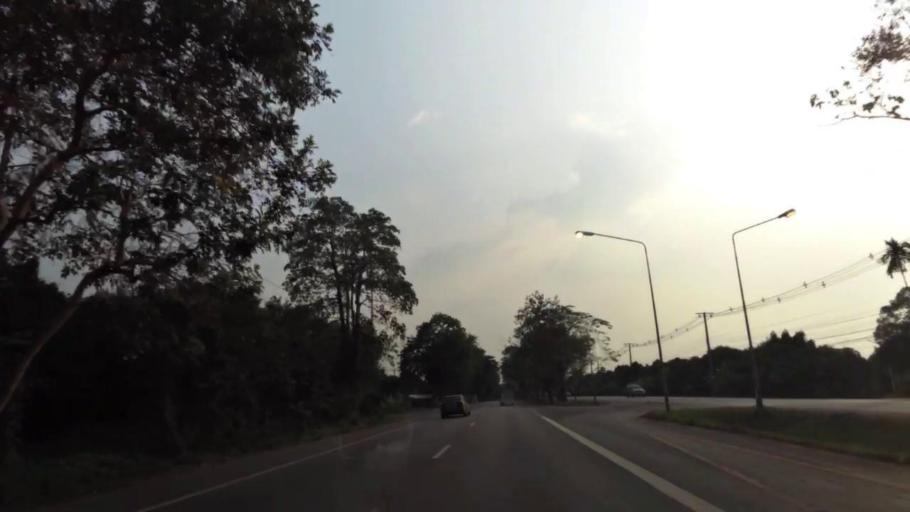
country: TH
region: Chanthaburi
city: Chanthaburi
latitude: 12.5674
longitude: 102.1618
